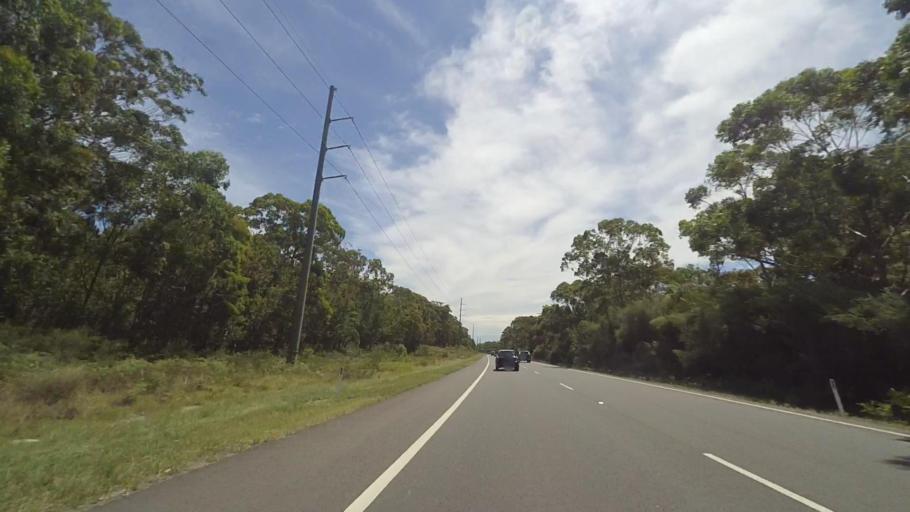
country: AU
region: New South Wales
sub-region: Port Stephens Shire
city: Anna Bay
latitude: -32.7807
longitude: 151.9920
